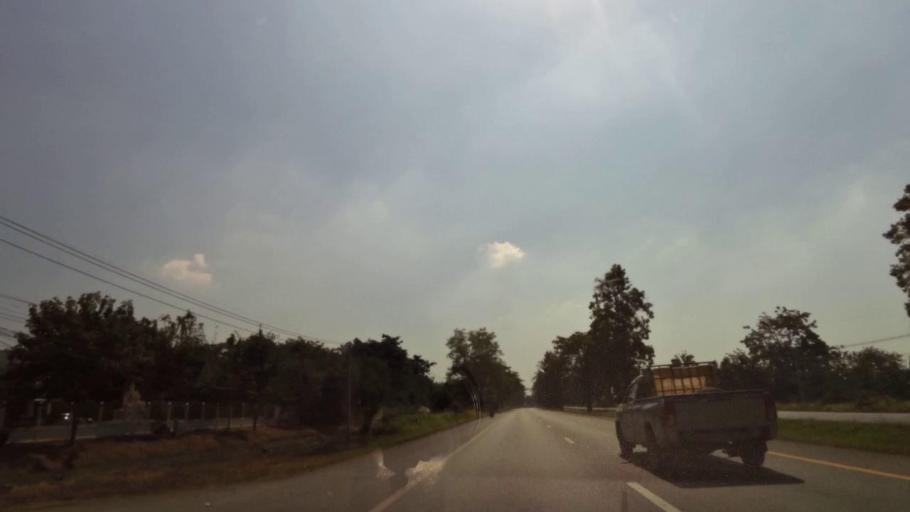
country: TH
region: Phichit
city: Bueng Na Rang
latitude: 16.1830
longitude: 100.1285
